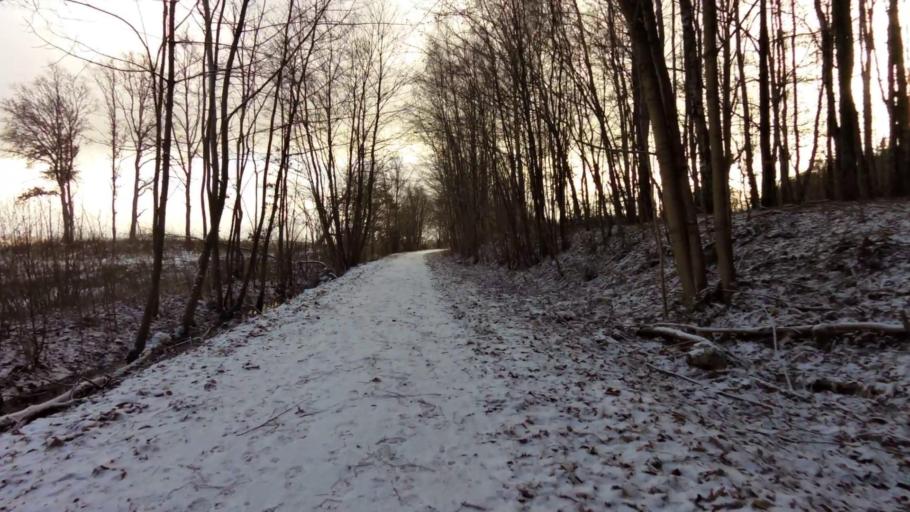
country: PL
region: West Pomeranian Voivodeship
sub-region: Powiat swidwinski
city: Polczyn-Zdroj
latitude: 53.7504
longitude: 16.0607
